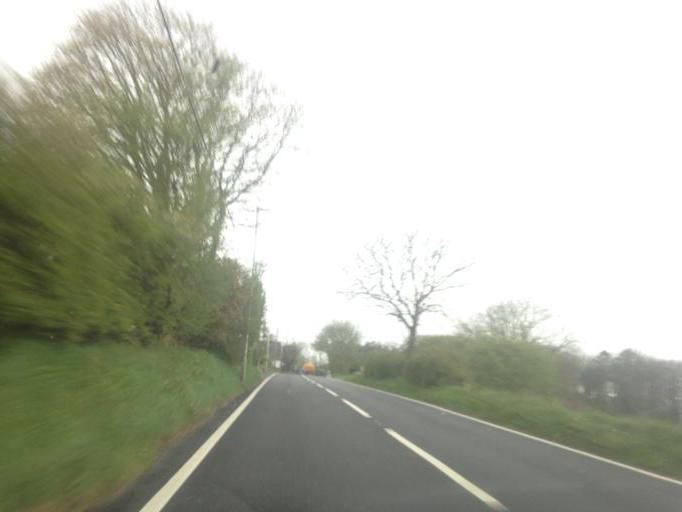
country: GB
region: Wales
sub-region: County of Ceredigion
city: Llanllwchaiarn
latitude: 52.1420
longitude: -4.4036
